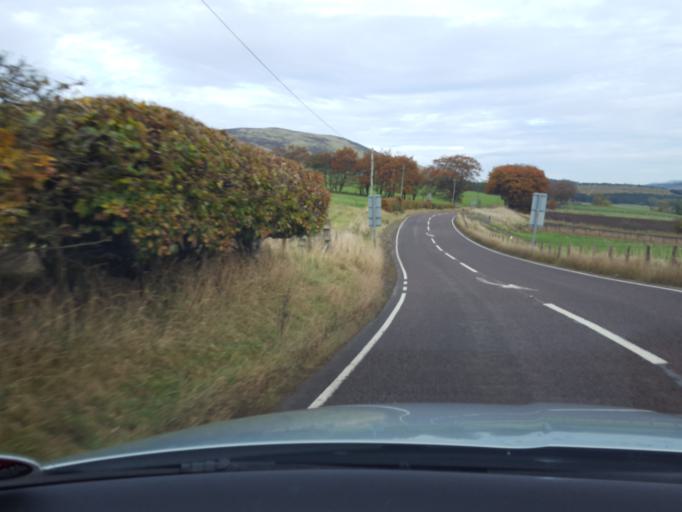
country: GB
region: Scotland
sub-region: South Lanarkshire
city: Biggar
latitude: 55.6778
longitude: -3.4864
